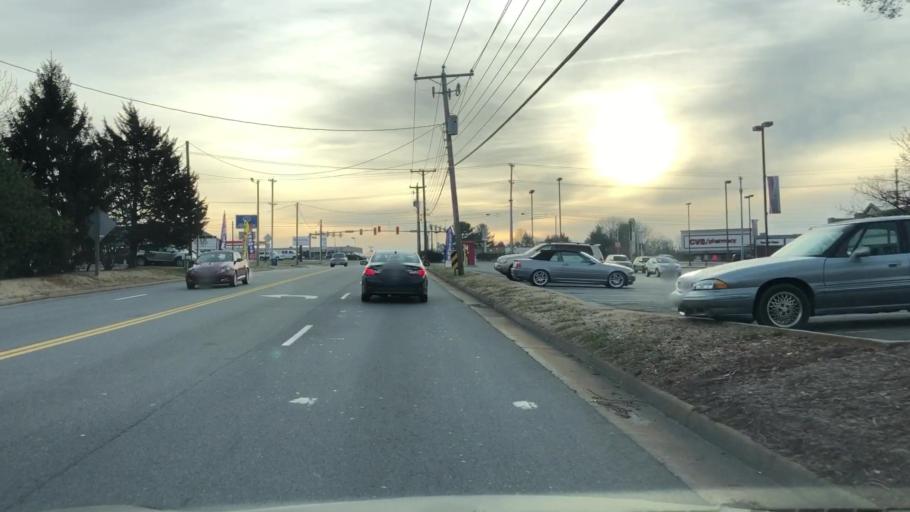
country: US
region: Virginia
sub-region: Campbell County
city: Timberlake
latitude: 37.3298
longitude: -79.2483
